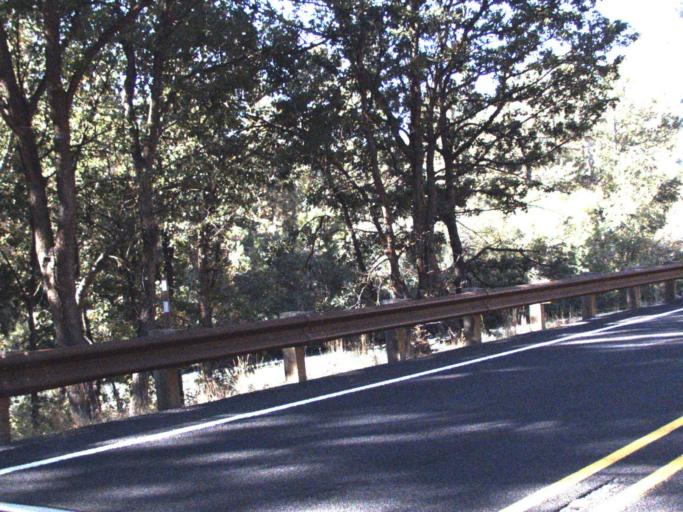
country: US
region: Washington
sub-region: Yakima County
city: Tieton
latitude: 46.7121
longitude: -120.8769
